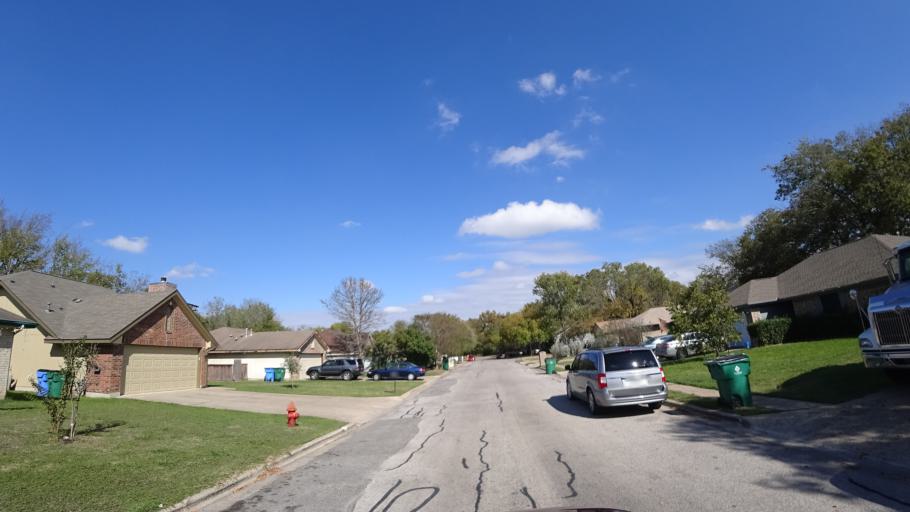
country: US
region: Texas
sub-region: Travis County
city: Windemere
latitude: 30.4529
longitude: -97.6425
